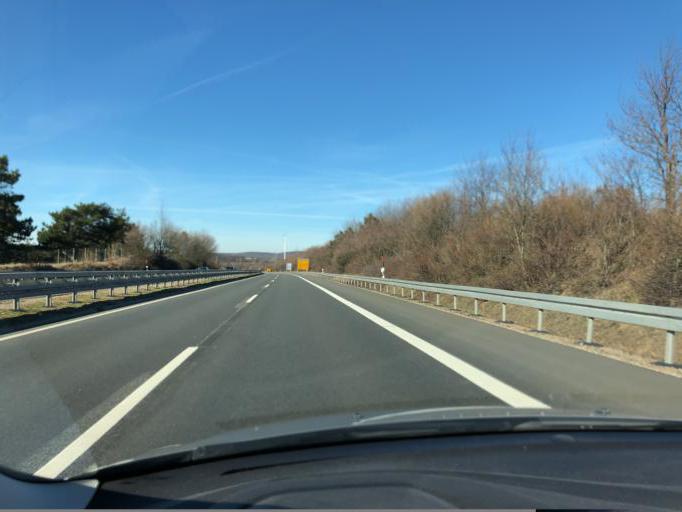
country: DE
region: Lower Saxony
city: Vienenburg
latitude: 51.9208
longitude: 10.5168
